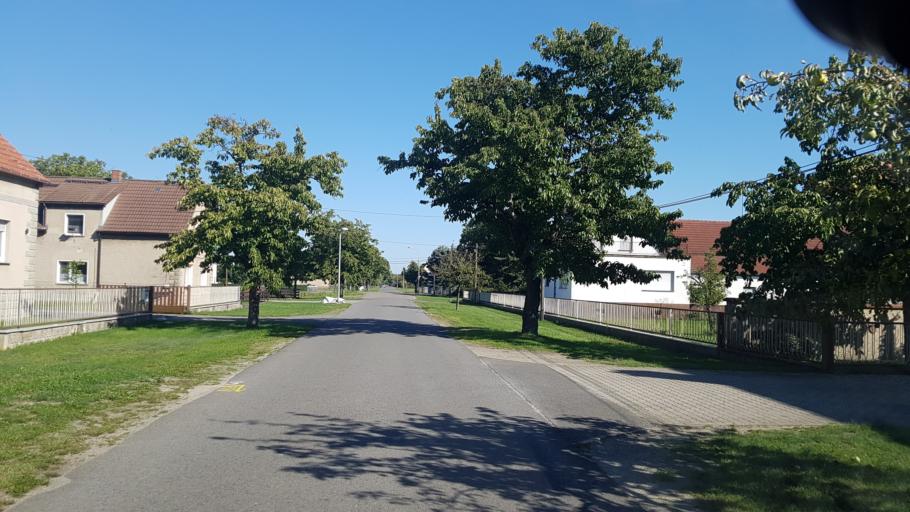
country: DE
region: Brandenburg
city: Schraden
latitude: 51.4227
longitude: 13.6875
